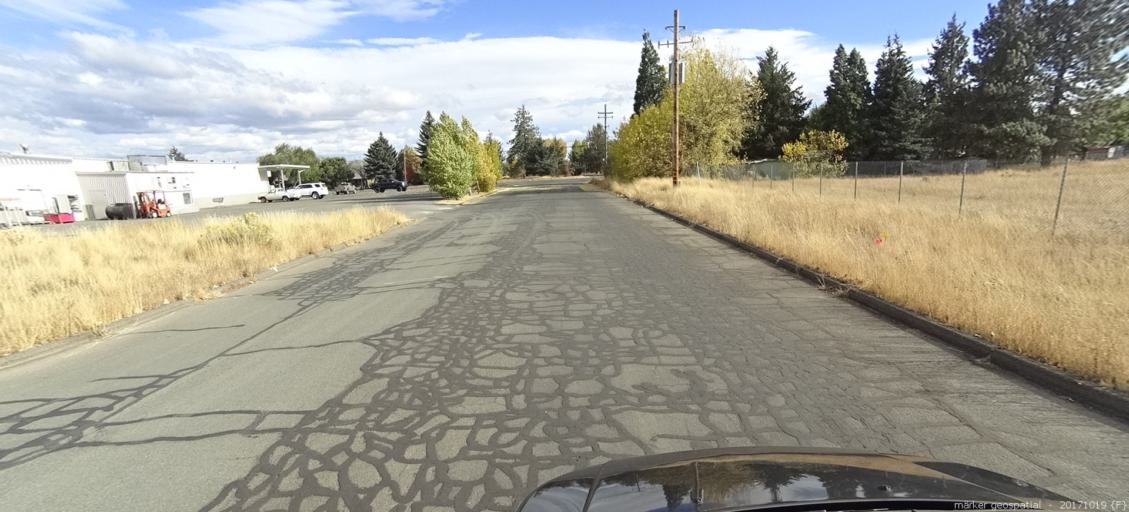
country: US
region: California
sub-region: Shasta County
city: Burney
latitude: 41.0274
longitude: -121.4231
